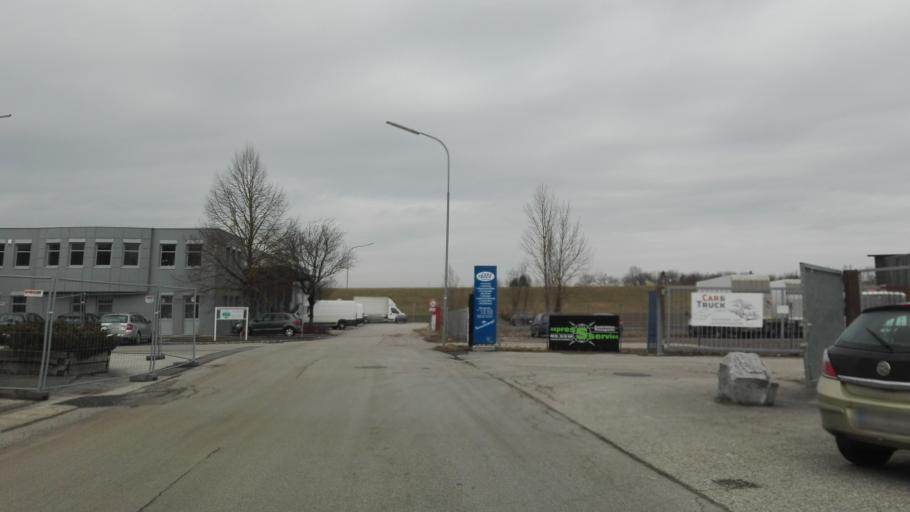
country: AT
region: Upper Austria
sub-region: Politischer Bezirk Linz-Land
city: Traun
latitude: 48.2315
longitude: 14.2162
